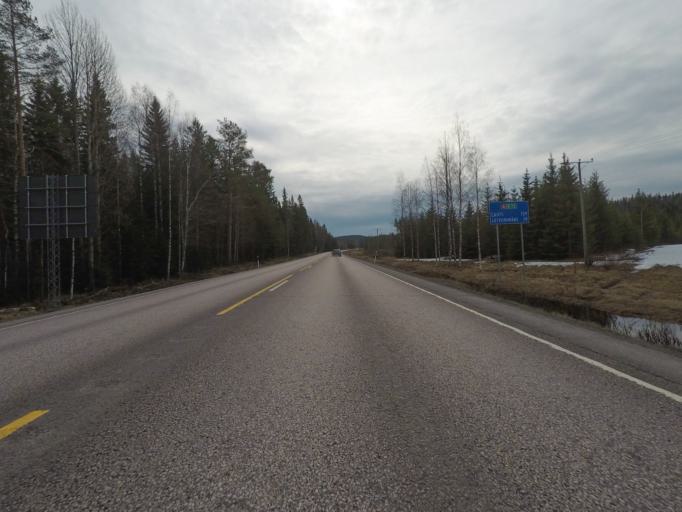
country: FI
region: Central Finland
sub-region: Jyvaeskylae
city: Toivakka
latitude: 62.0676
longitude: 26.0439
